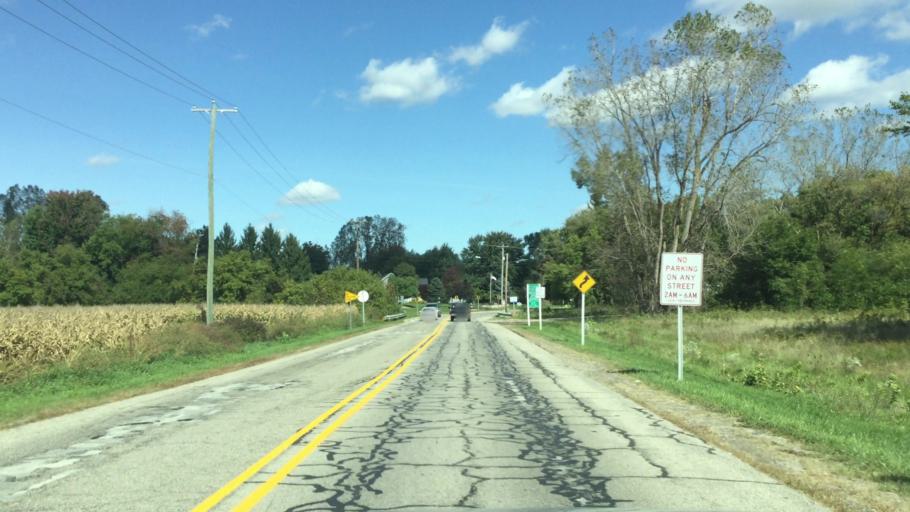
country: US
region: Michigan
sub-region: Genesee County
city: Swartz Creek
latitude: 42.9436
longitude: -83.8581
